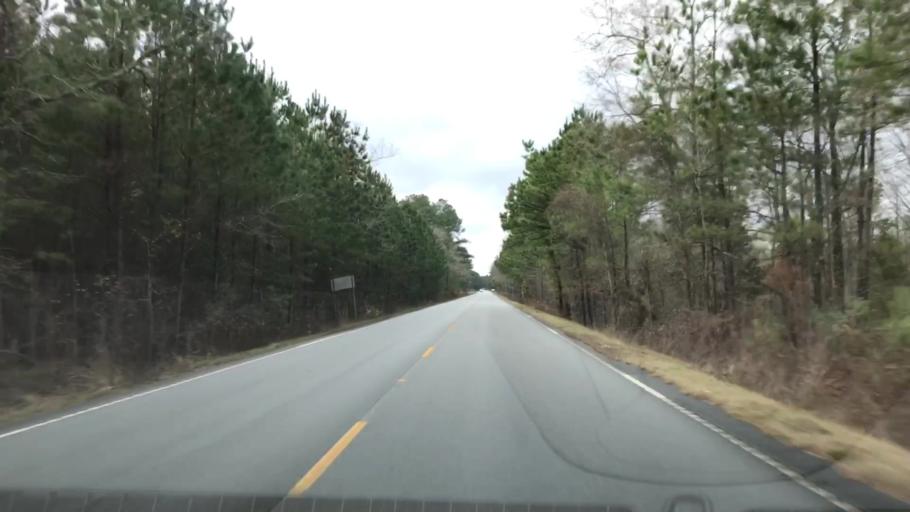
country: US
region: South Carolina
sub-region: Berkeley County
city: Saint Stephen
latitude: 33.2873
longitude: -79.7597
